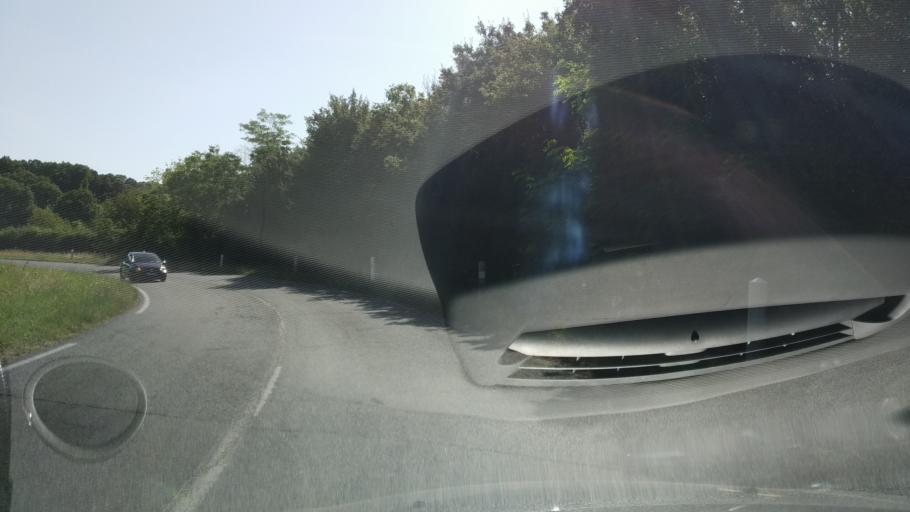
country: FR
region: Poitou-Charentes
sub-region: Departement de la Vienne
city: Lussac-les-Chateaux
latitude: 46.4619
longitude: 0.6469
